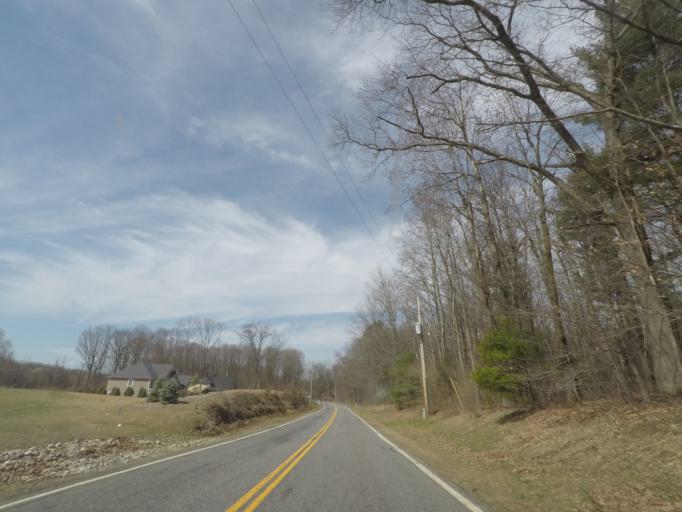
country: US
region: New York
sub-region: Saratoga County
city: Country Knolls
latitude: 42.9062
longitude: -73.7576
